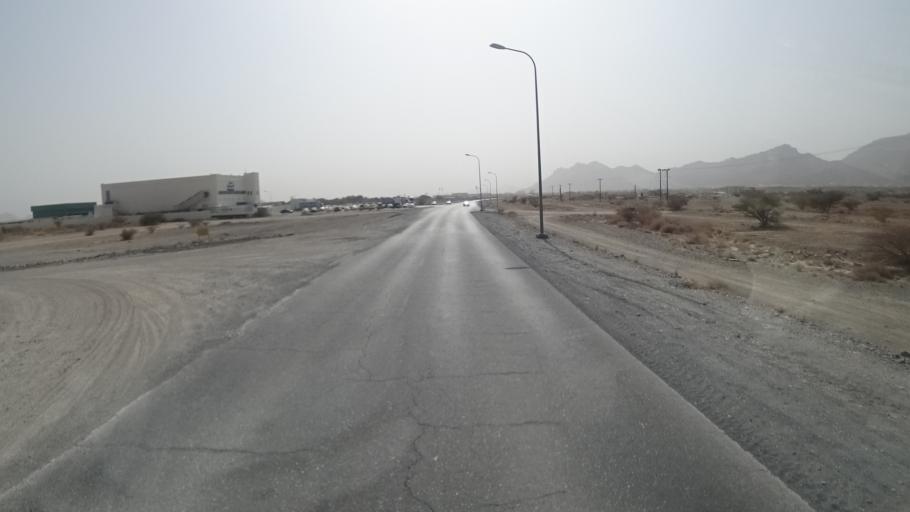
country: OM
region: Muhafazat ad Dakhiliyah
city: Nizwa
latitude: 22.9169
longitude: 57.6100
